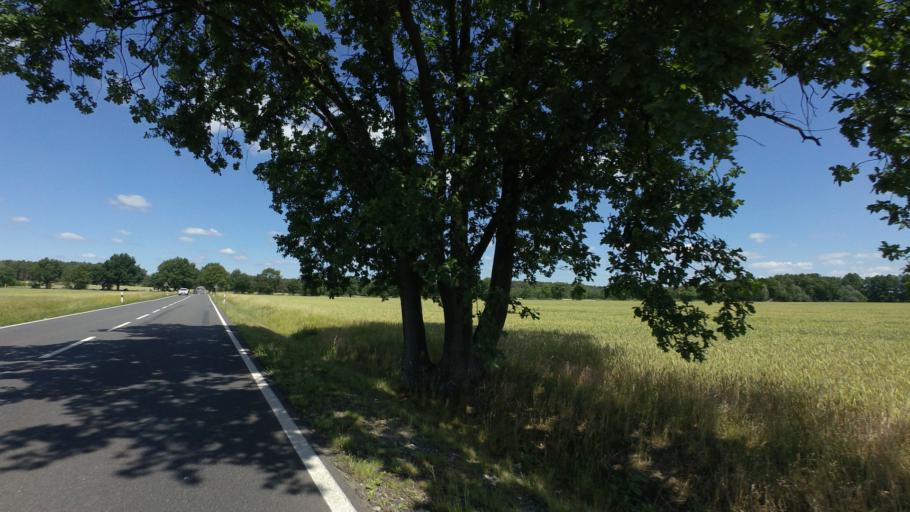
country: DE
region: Brandenburg
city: Kasel-Golzig
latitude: 51.9053
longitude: 13.6739
